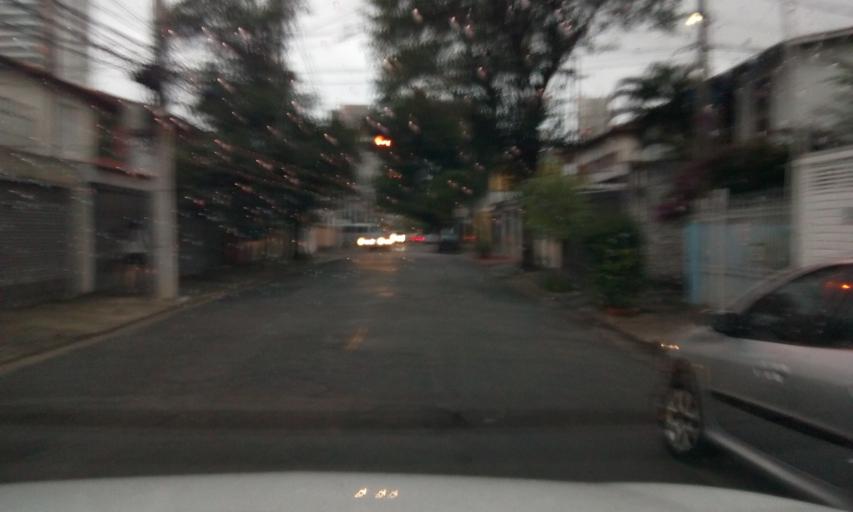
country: BR
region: Sao Paulo
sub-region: Sao Paulo
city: Sao Paulo
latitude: -23.6104
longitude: -46.6911
